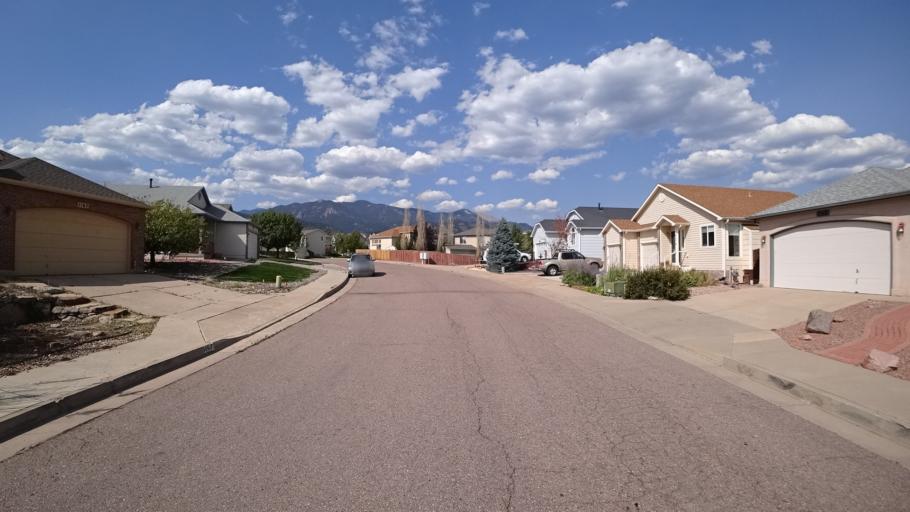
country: US
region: Colorado
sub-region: El Paso County
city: Colorado Springs
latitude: 38.8270
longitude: -104.8478
